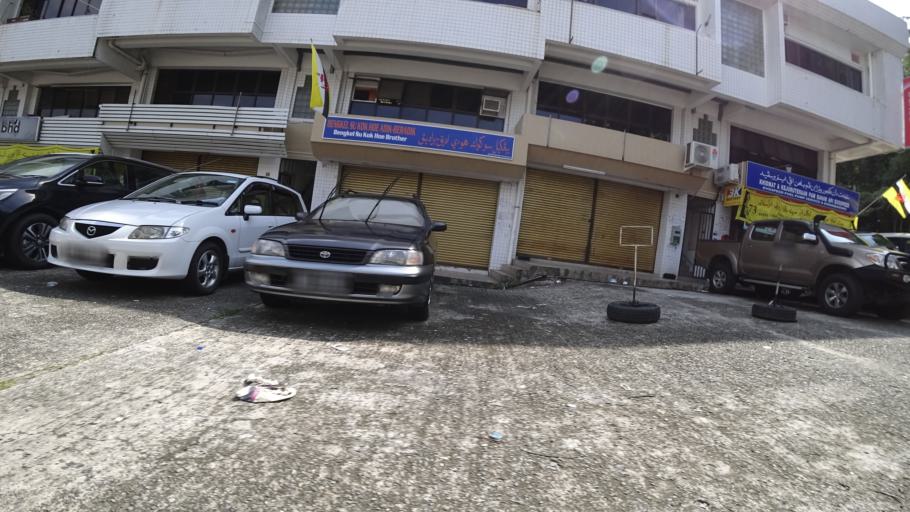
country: BN
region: Brunei and Muara
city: Bandar Seri Begawan
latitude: 4.8578
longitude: 114.8918
